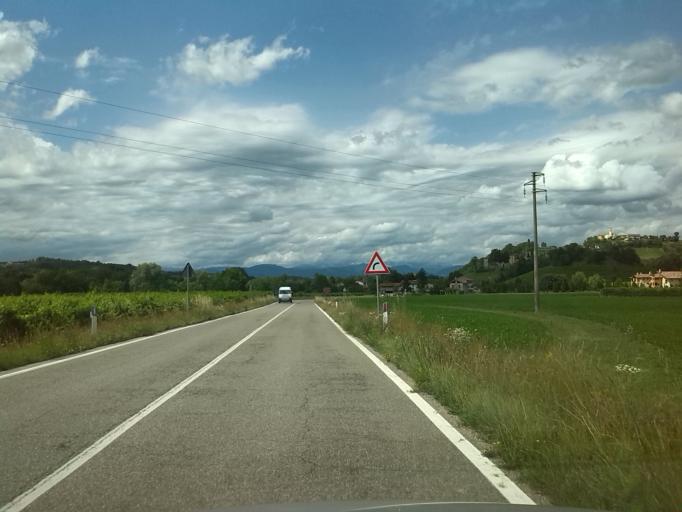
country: IT
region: Friuli Venezia Giulia
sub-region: Provincia di Udine
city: Corno di Rosazzo
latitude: 45.9850
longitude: 13.4672
